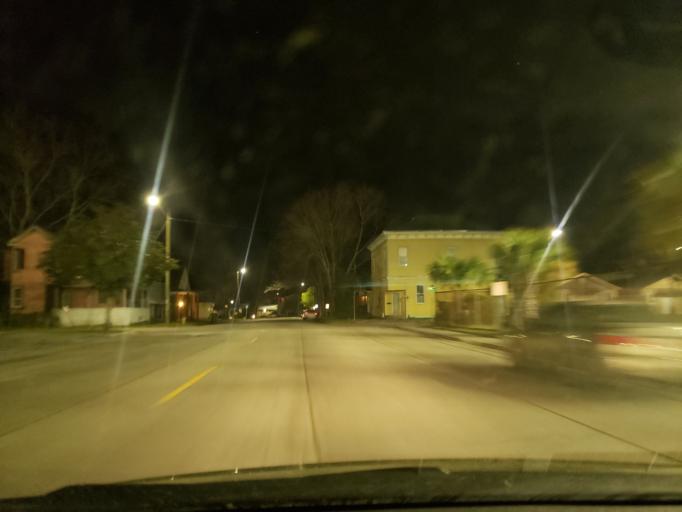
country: US
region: Georgia
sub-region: Chatham County
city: Savannah
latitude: 32.0634
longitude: -81.0817
